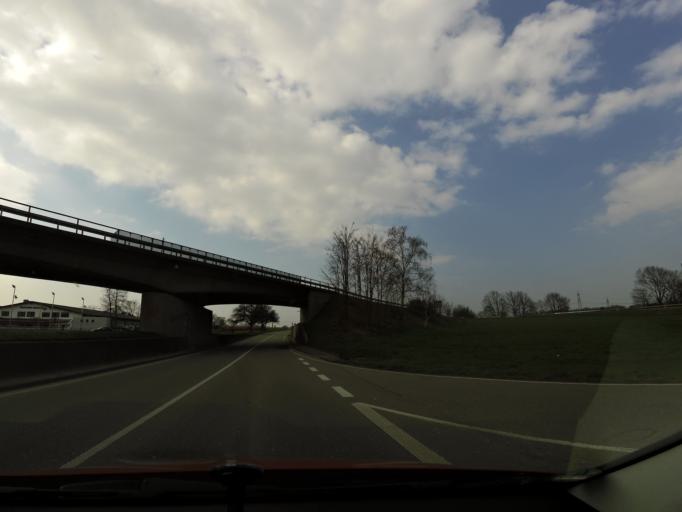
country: DE
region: Baden-Wuerttemberg
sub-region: Freiburg Region
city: Achern
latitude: 48.6378
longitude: 8.0451
